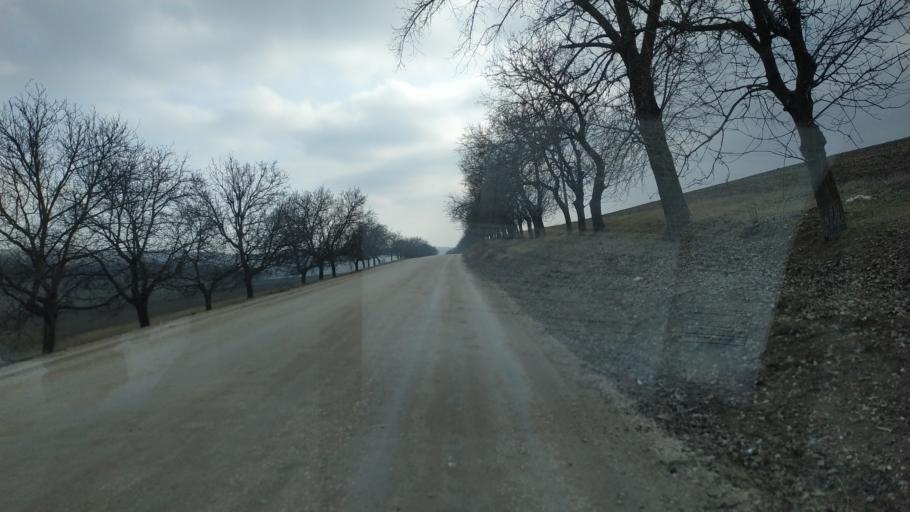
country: MD
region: Hincesti
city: Dancu
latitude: 46.9255
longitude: 28.3280
